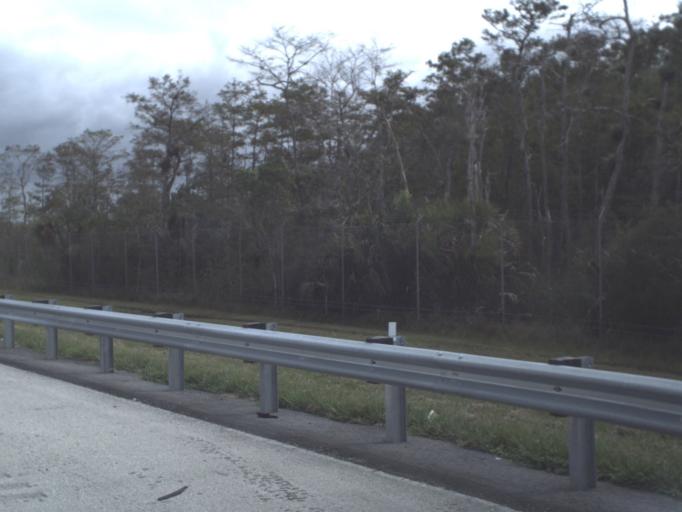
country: US
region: Florida
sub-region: Collier County
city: Immokalee
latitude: 26.1702
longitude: -80.9870
